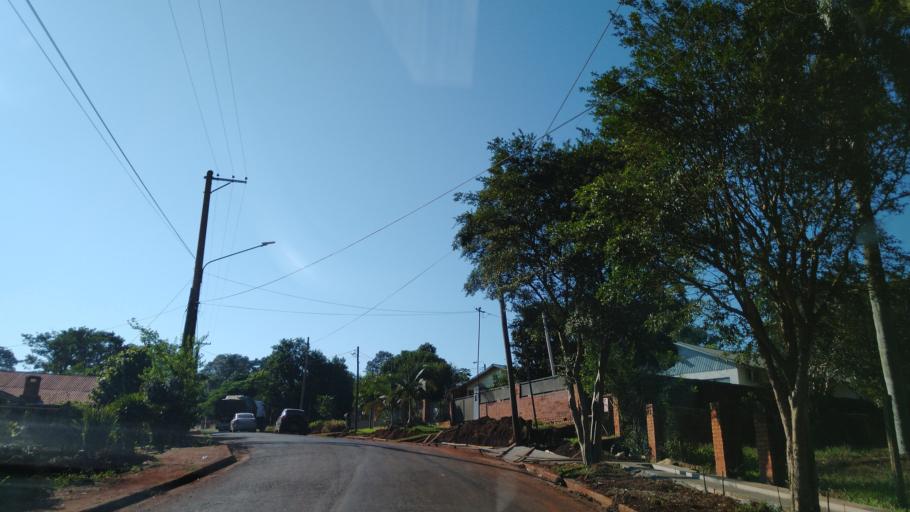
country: AR
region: Misiones
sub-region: Departamento de Montecarlo
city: Montecarlo
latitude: -26.5645
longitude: -54.7713
